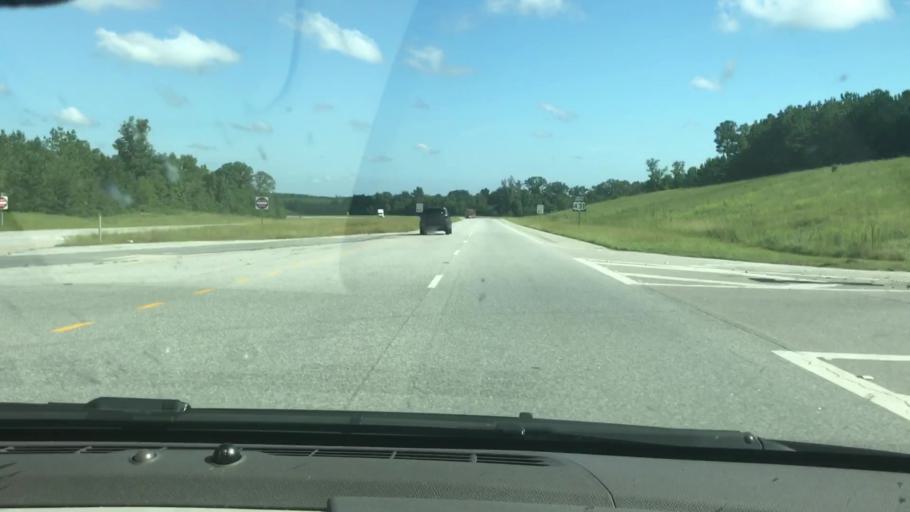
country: US
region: Alabama
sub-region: Barbour County
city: Eufaula
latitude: 32.1659
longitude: -85.1764
